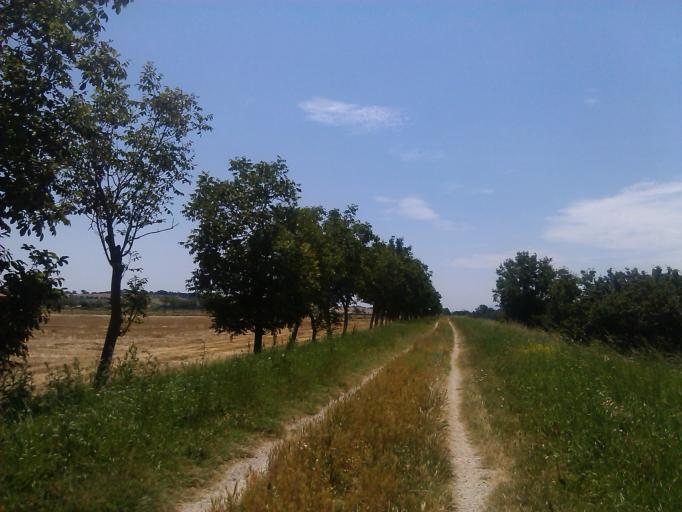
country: IT
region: Tuscany
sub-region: Province of Arezzo
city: Cesa
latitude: 43.3071
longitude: 11.8392
